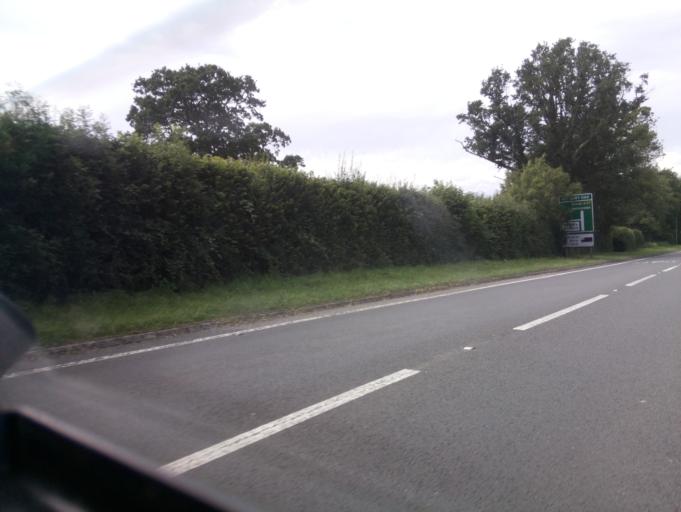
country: GB
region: England
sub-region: Somerset
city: Yeovil
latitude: 50.8686
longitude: -2.5958
